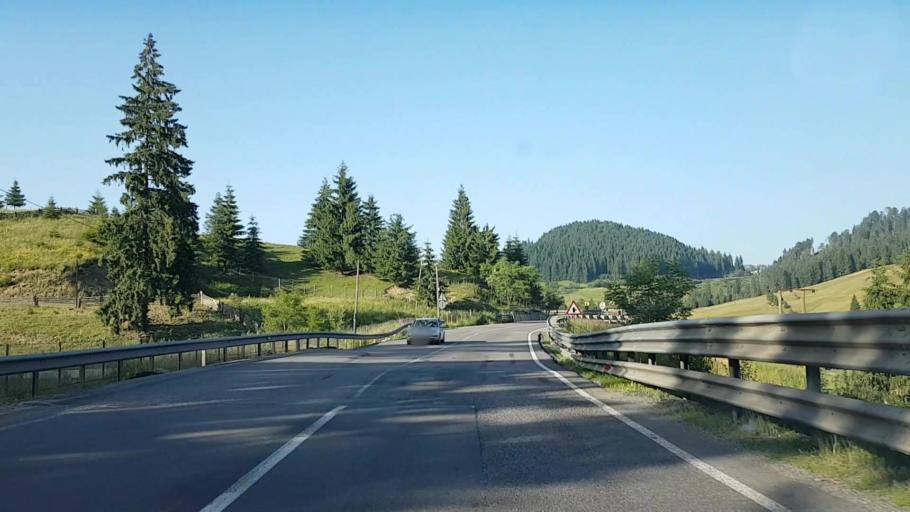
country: RO
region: Bistrita-Nasaud
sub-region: Comuna Lunca Ilvei
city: Lunca Ilvei
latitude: 47.2224
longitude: 24.9539
